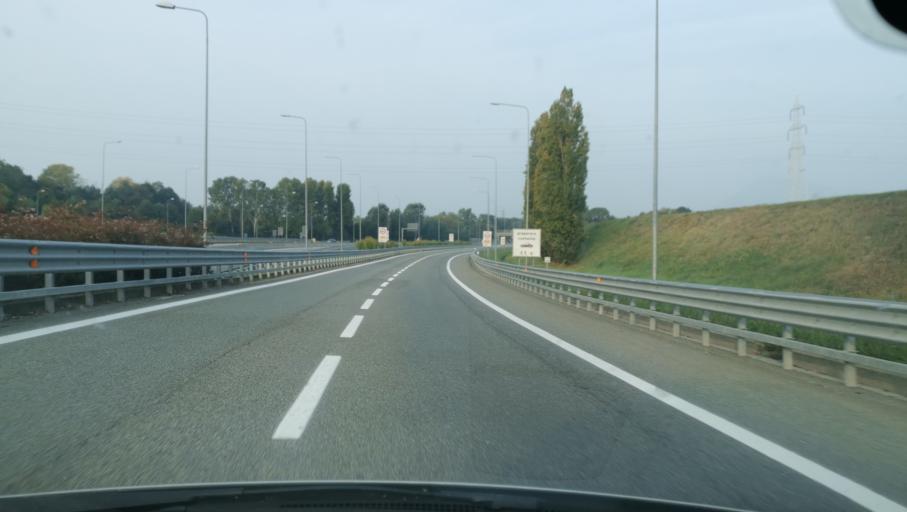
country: IT
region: Piedmont
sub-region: Provincia di Torino
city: Pianezza
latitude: 45.0811
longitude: 7.5485
